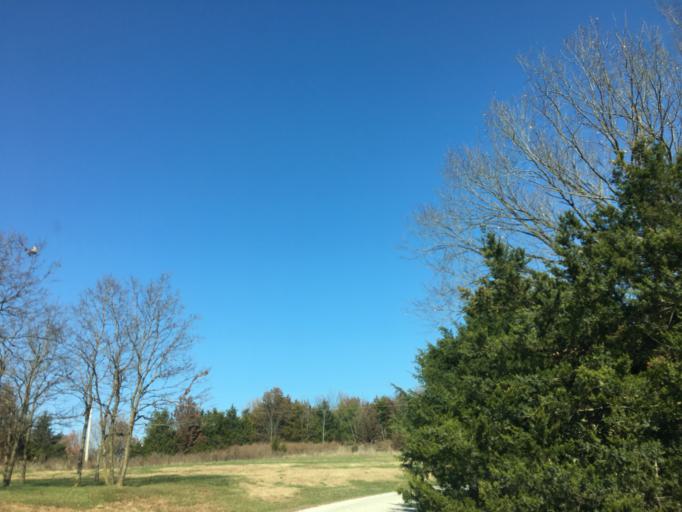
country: US
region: Missouri
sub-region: Cole County
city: Wardsville
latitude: 38.4821
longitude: -92.1783
